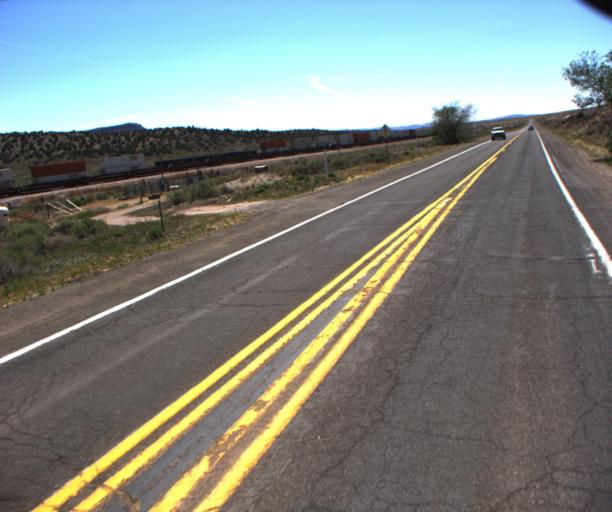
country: US
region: Arizona
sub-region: Mohave County
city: Peach Springs
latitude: 35.5280
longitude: -113.4302
